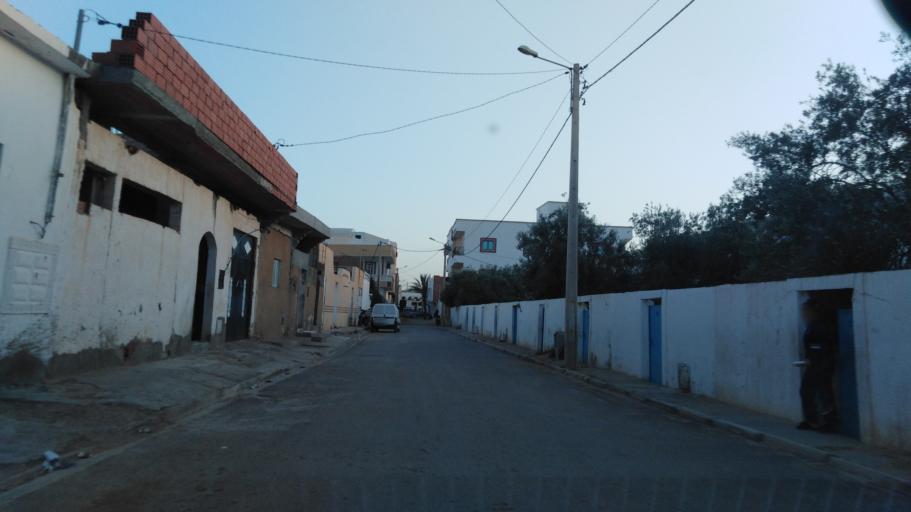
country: TN
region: Tataouine
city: Tataouine
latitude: 32.9394
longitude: 10.4571
